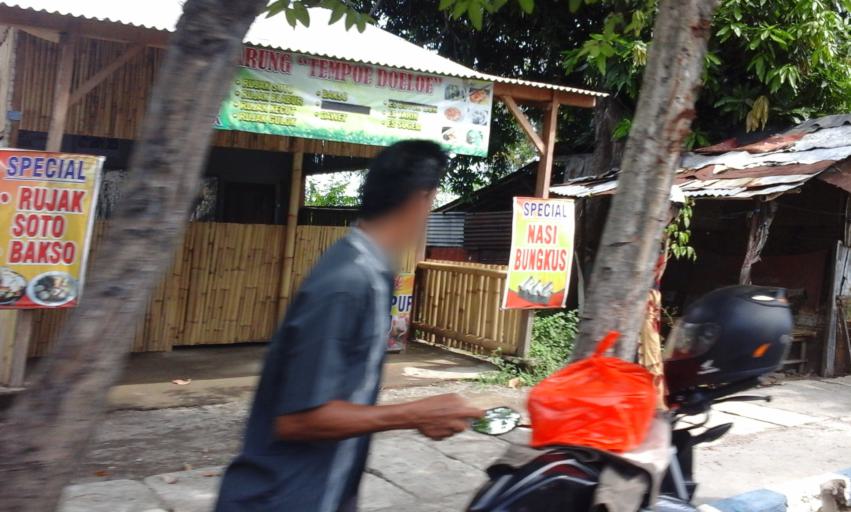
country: ID
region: East Java
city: Krajan Satu
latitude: -8.2086
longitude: 114.3564
